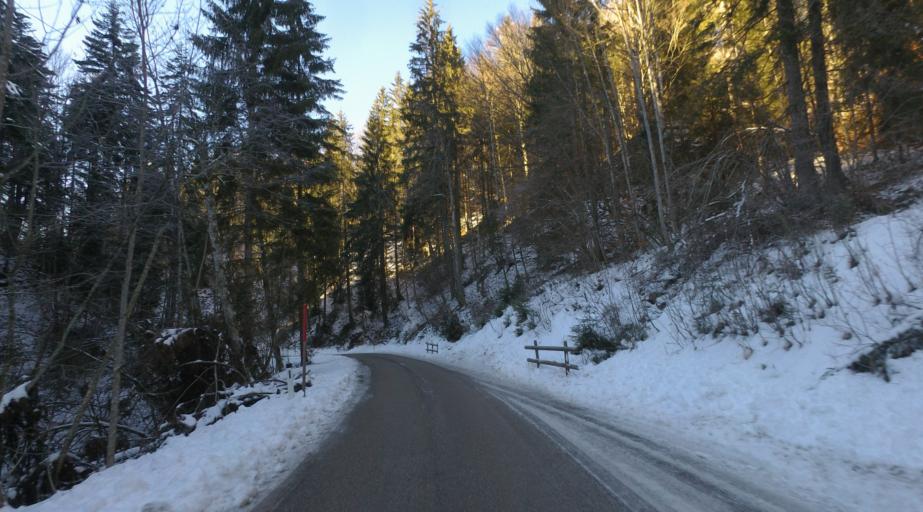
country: AT
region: Tyrol
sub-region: Politischer Bezirk Kitzbuhel
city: Kossen
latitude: 47.6757
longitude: 12.4274
